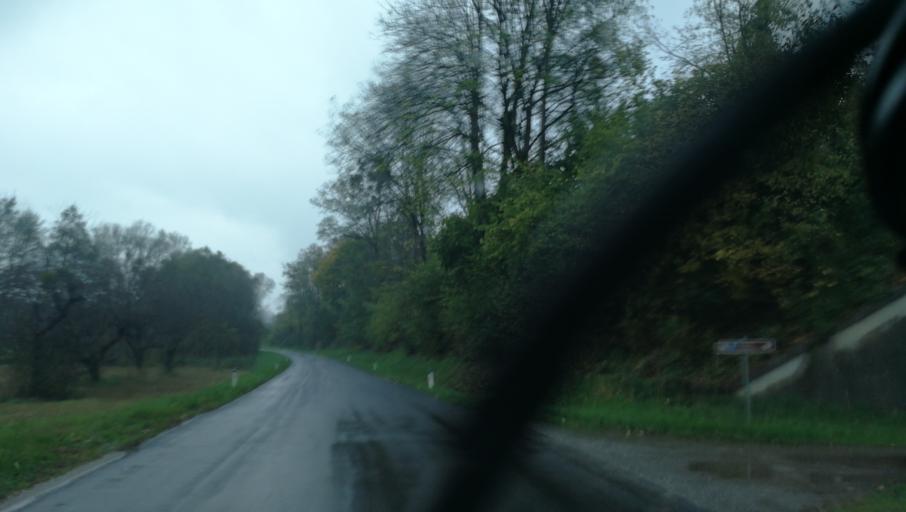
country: AT
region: Styria
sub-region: Politischer Bezirk Leibnitz
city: Spielfeld
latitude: 46.7125
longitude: 15.6251
